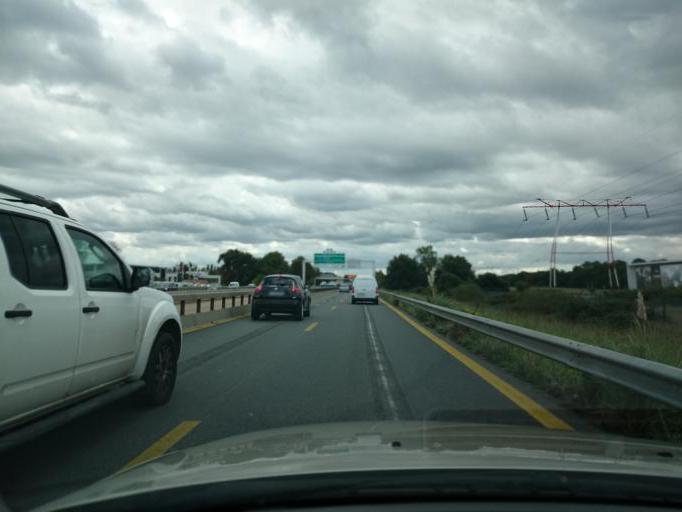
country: FR
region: Aquitaine
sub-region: Departement de la Gironde
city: Pessac
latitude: 44.8270
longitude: -0.6754
